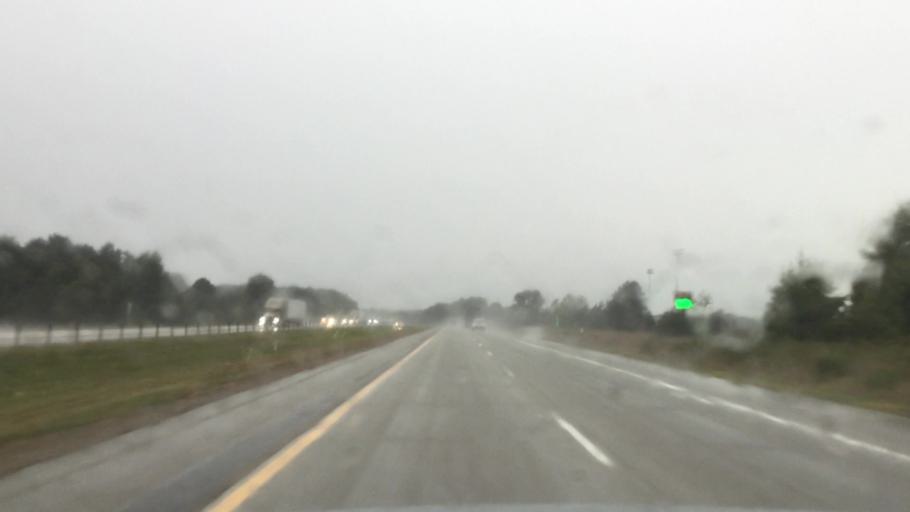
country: US
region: Michigan
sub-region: Van Buren County
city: Paw Paw
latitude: 42.2182
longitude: -85.8470
